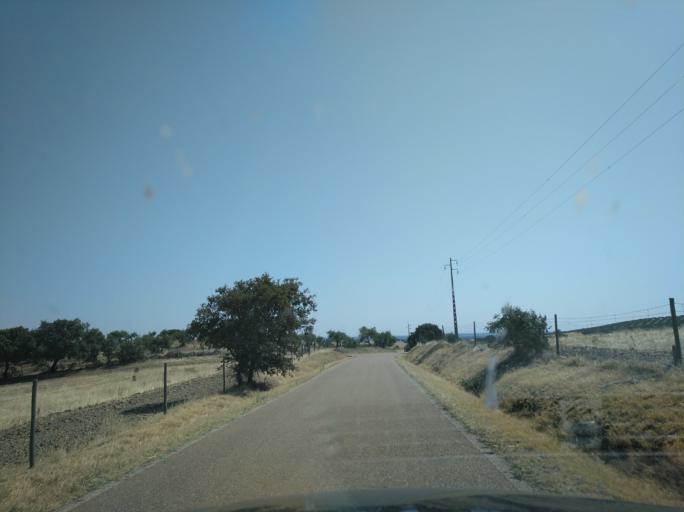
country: PT
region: Portalegre
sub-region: Campo Maior
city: Campo Maior
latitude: 39.0287
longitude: -7.0202
